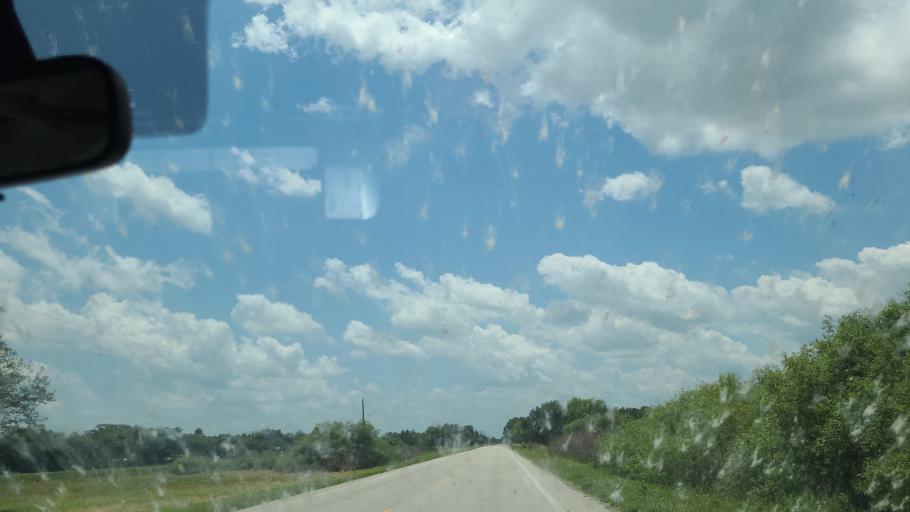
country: US
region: Florida
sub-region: Glades County
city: Buckhead Ridge
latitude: 27.0936
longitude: -81.0702
